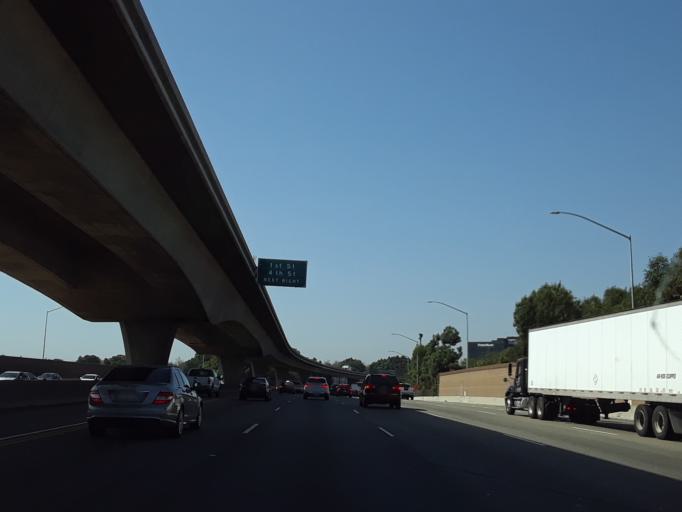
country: US
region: California
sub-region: Orange County
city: Tustin
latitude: 33.7419
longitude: -117.8370
